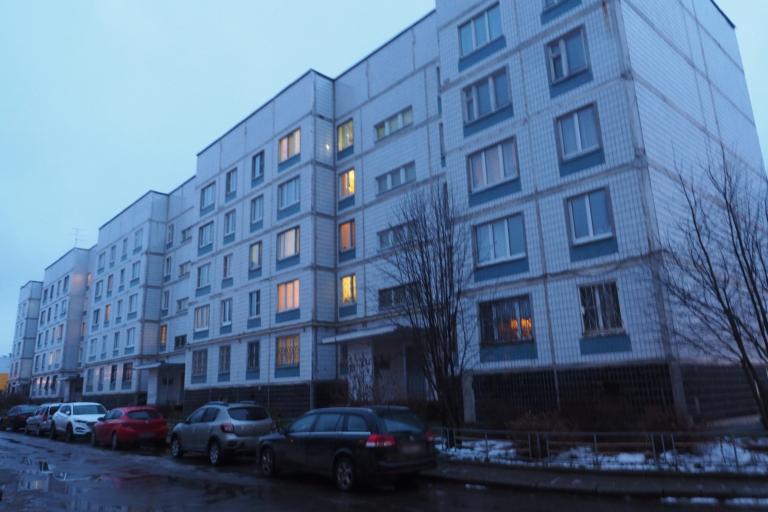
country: RU
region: Moskovskaya
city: Sergiyev Posad
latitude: 56.3347
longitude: 38.1404
